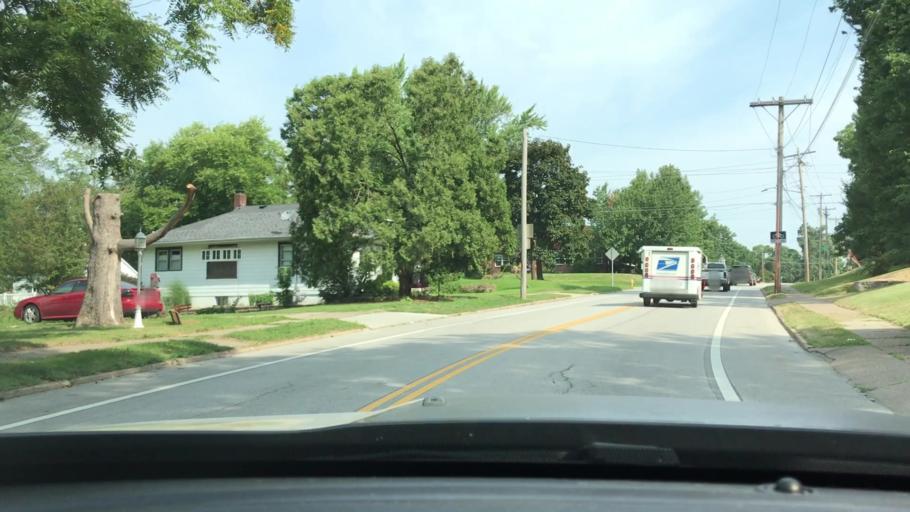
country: US
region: Iowa
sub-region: Scott County
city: Bettendorf
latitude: 41.5408
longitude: -90.5417
